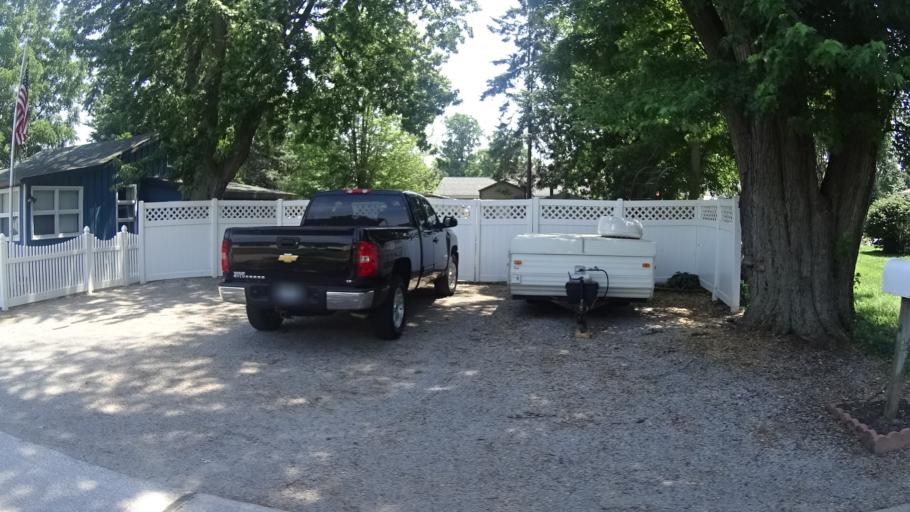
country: US
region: Ohio
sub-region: Erie County
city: Huron
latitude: 41.4116
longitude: -82.5887
